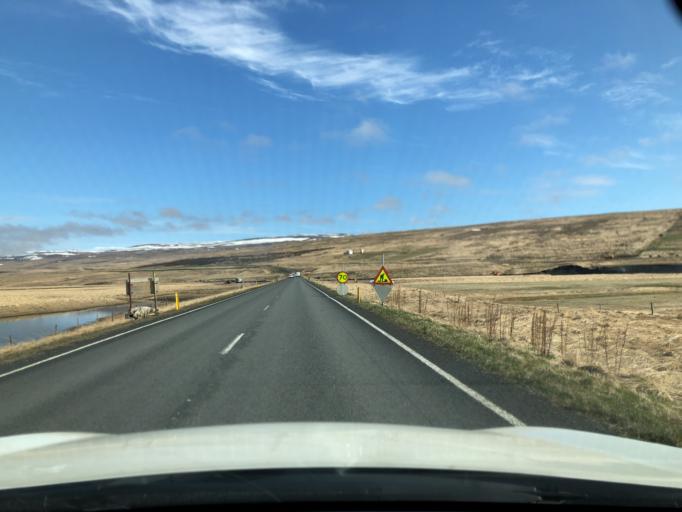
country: IS
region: West
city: Borgarnes
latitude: 65.3272
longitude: -20.9053
